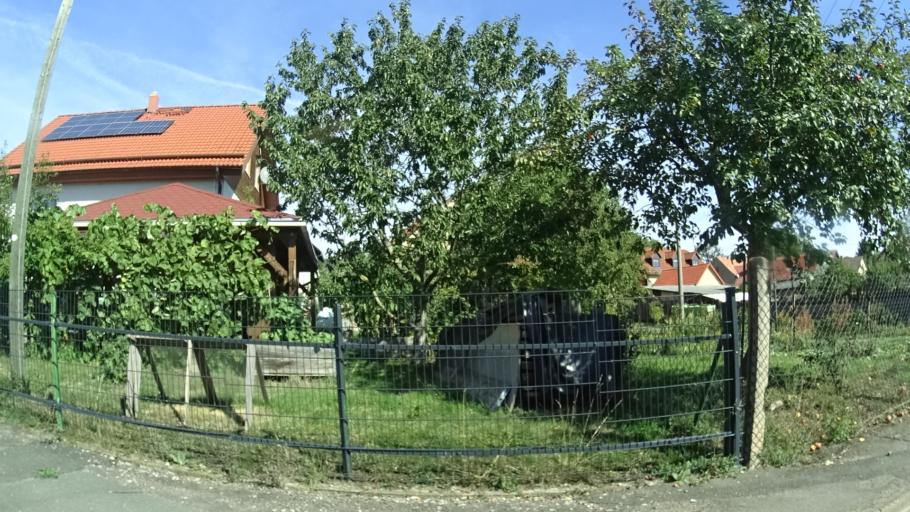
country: DE
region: Thuringia
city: Rittersdorf
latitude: 50.7486
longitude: 11.2125
